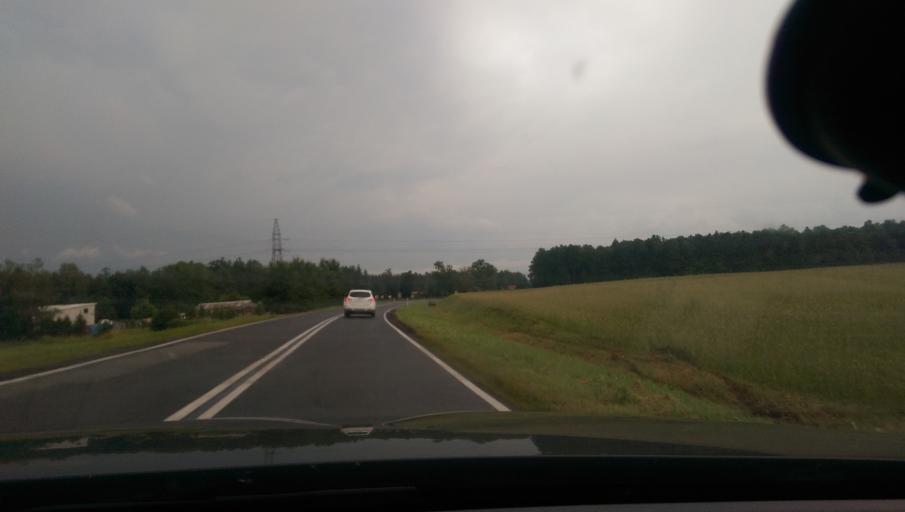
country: PL
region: Warmian-Masurian Voivodeship
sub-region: Powiat szczycienski
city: Szczytno
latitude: 53.5432
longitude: 20.9893
